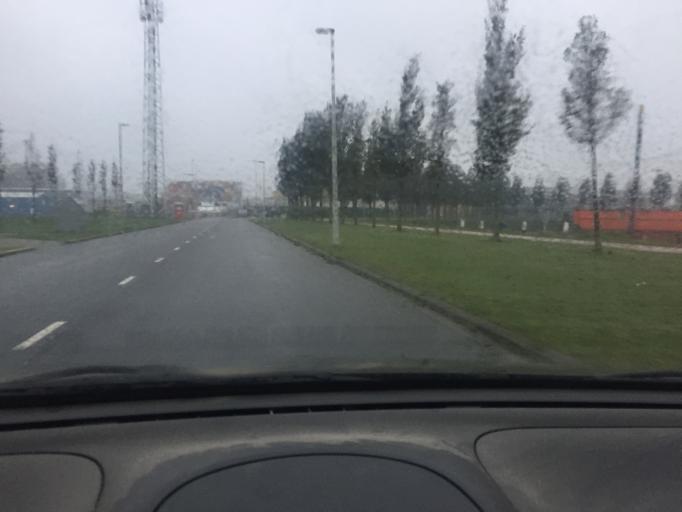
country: NL
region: South Holland
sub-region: Gemeente Schiedam
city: Schiedam
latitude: 51.8935
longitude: 4.4128
